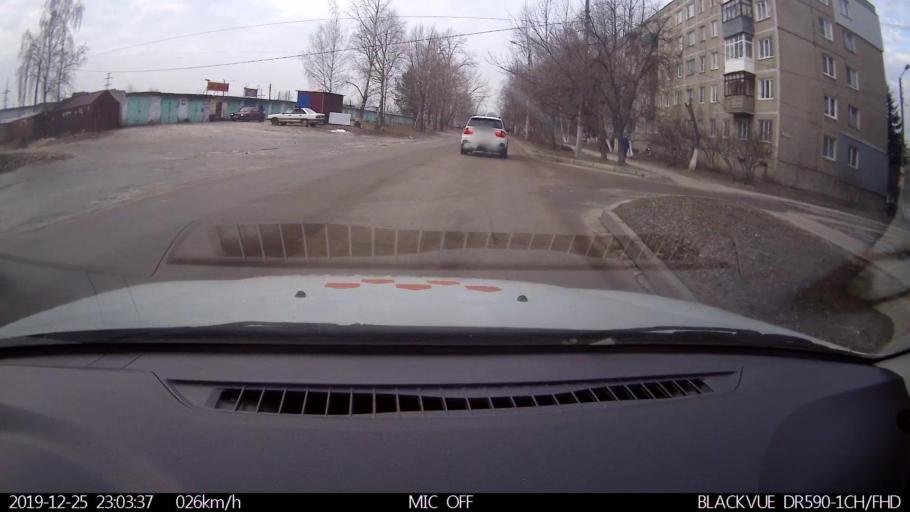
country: RU
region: Nizjnij Novgorod
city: Gorbatovka
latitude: 56.3553
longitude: 43.8198
